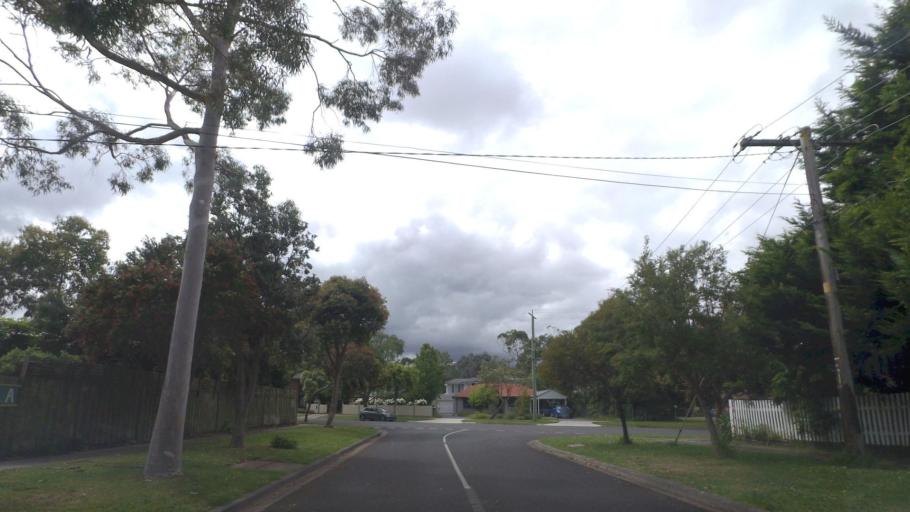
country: AU
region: Victoria
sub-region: Maroondah
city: Croydon North
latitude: -37.7863
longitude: 145.2883
